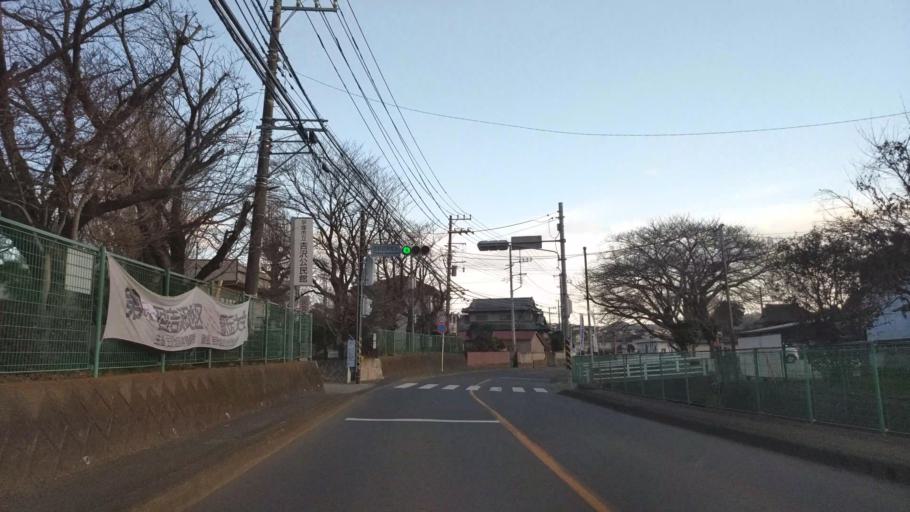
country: JP
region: Kanagawa
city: Oiso
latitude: 35.3439
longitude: 139.2906
